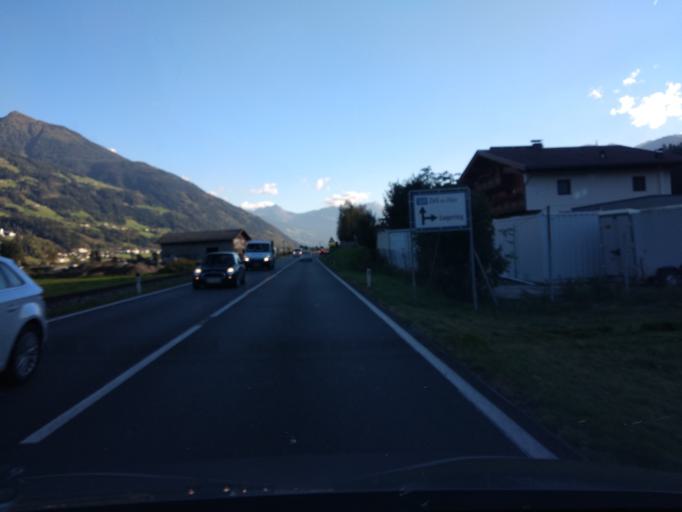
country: AT
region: Tyrol
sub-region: Politischer Bezirk Schwaz
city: Fugenberg
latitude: 47.3644
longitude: 11.8510
